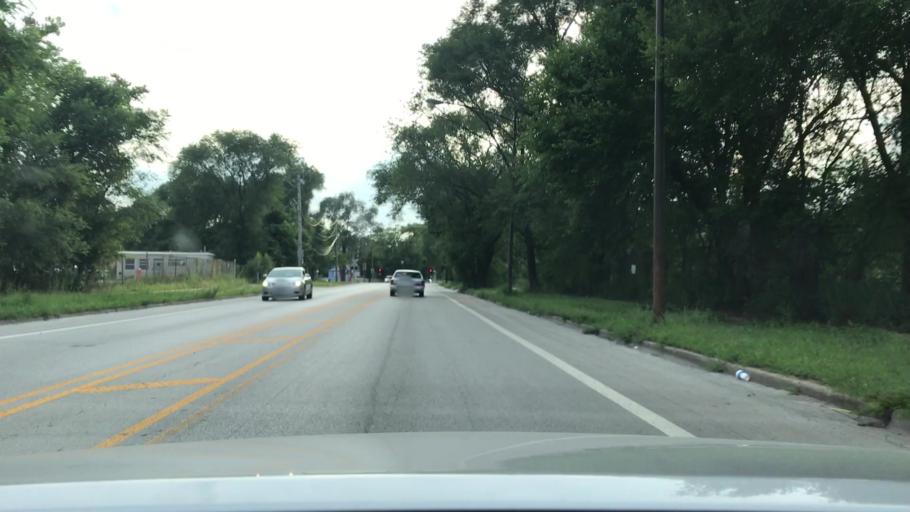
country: US
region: Indiana
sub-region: Lake County
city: Whiting
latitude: 41.7134
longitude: -87.5570
